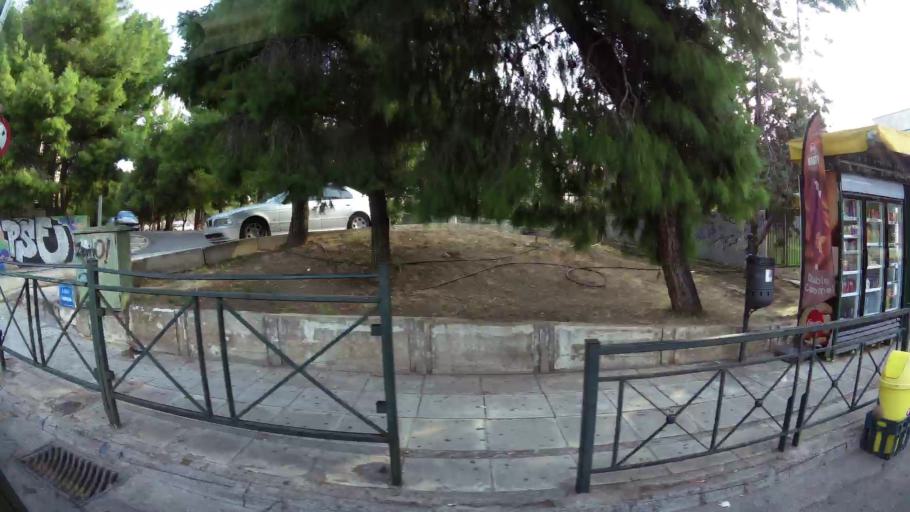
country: GR
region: Attica
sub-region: Nomarchia Athinas
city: Nea Chalkidona
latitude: 38.0280
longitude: 23.7307
